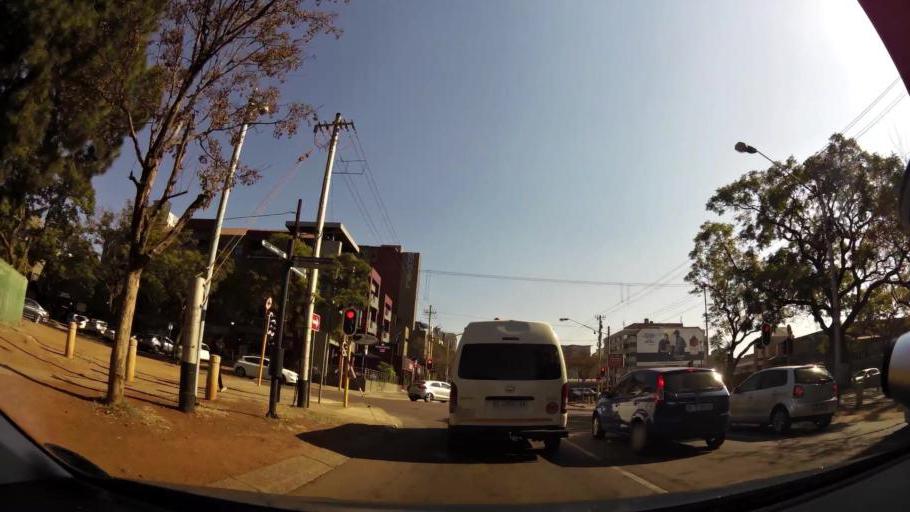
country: ZA
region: Gauteng
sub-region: City of Tshwane Metropolitan Municipality
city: Pretoria
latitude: -25.7504
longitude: 28.2378
